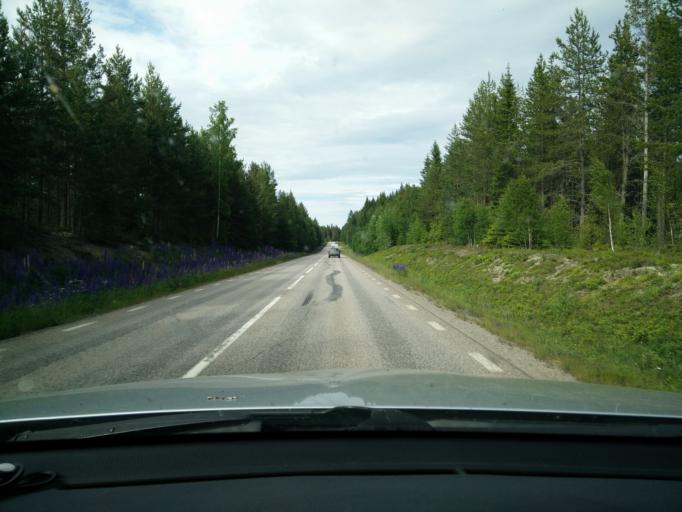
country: SE
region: Gaevleborg
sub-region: Nordanstigs Kommun
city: Bergsjoe
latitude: 61.9306
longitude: 17.0335
